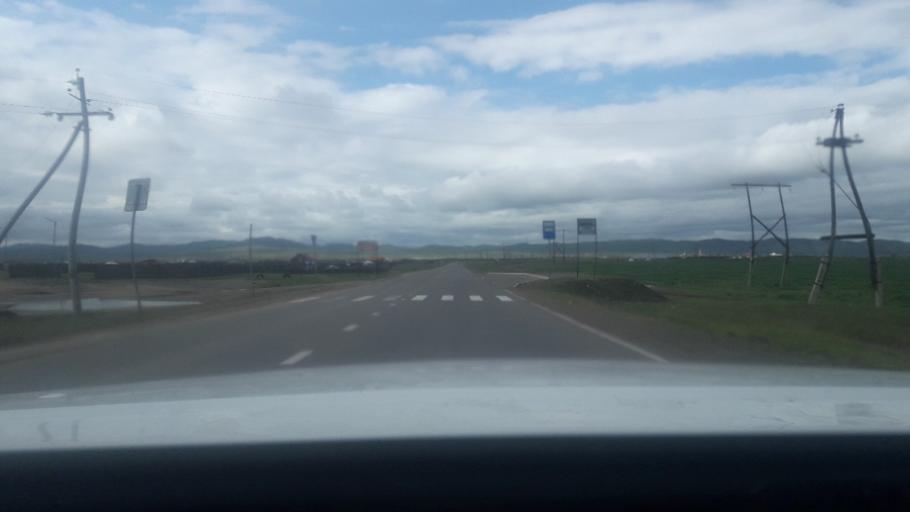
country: MN
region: Central Aimak
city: Altanbulag
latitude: 47.7687
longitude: 106.6012
